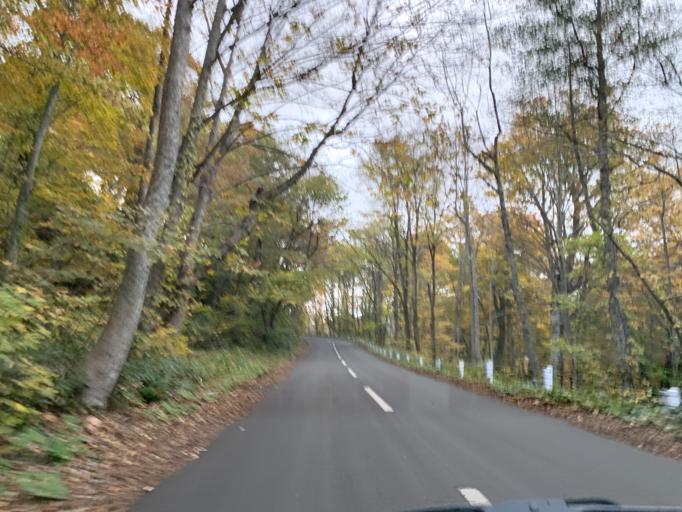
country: JP
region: Iwate
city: Mizusawa
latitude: 39.1051
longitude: 140.8706
